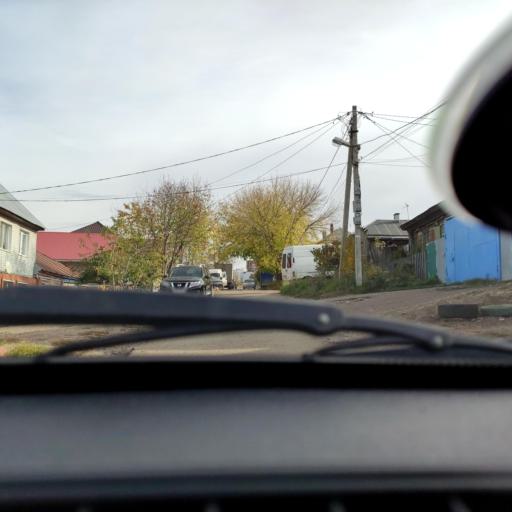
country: RU
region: Bashkortostan
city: Ufa
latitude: 54.7279
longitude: 55.9175
